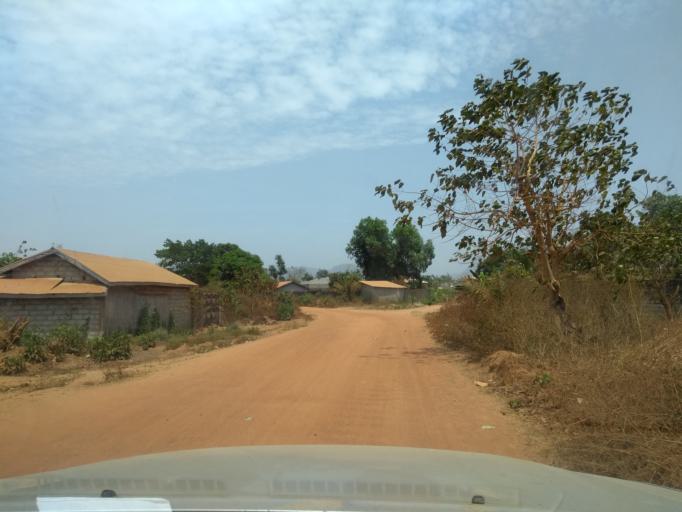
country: GN
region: Kindia
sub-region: Prefecture de Dubreka
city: Dubreka
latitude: 9.7865
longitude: -13.5373
